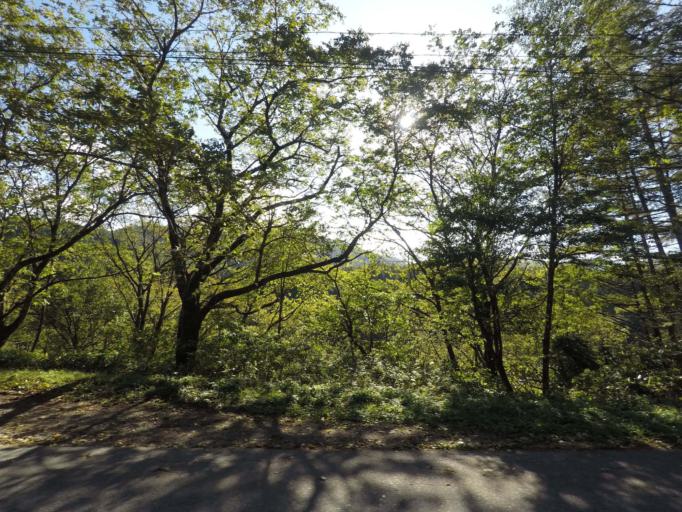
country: JP
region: Nagano
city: Ina
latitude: 35.9494
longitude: 137.7819
